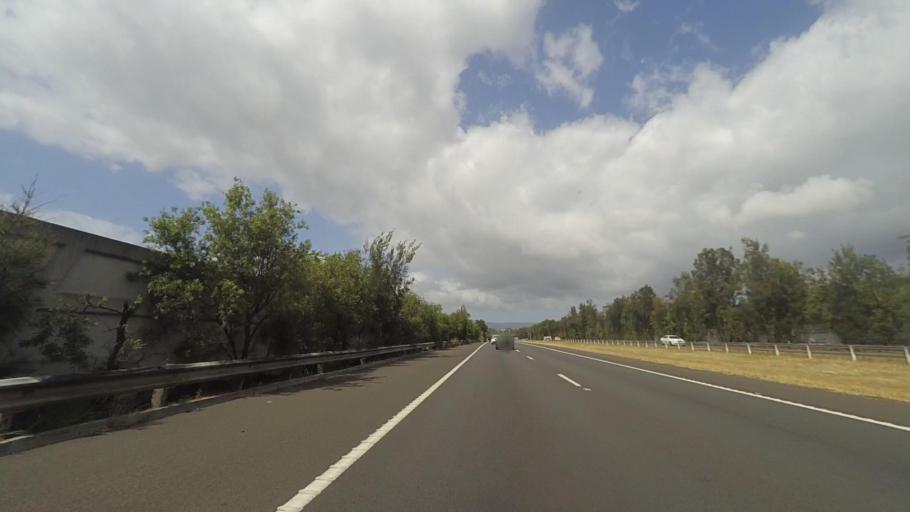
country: AU
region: New South Wales
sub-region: Wollongong
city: Koonawarra
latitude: -34.4951
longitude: 150.8013
